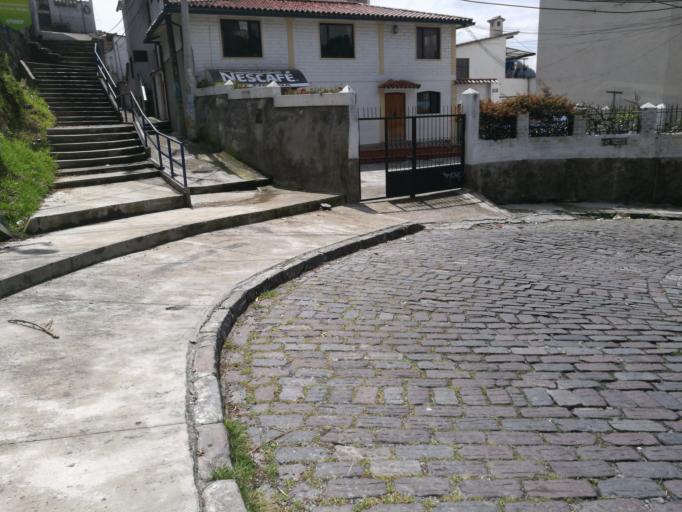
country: EC
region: Pichincha
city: Quito
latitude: -0.2017
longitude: -78.4786
